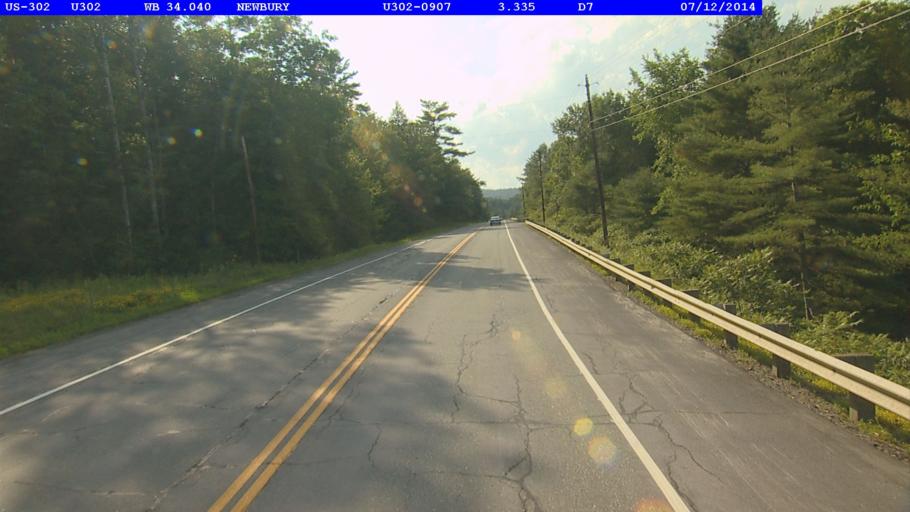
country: US
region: New Hampshire
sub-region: Grafton County
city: Woodsville
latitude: 44.1507
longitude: -72.0692
